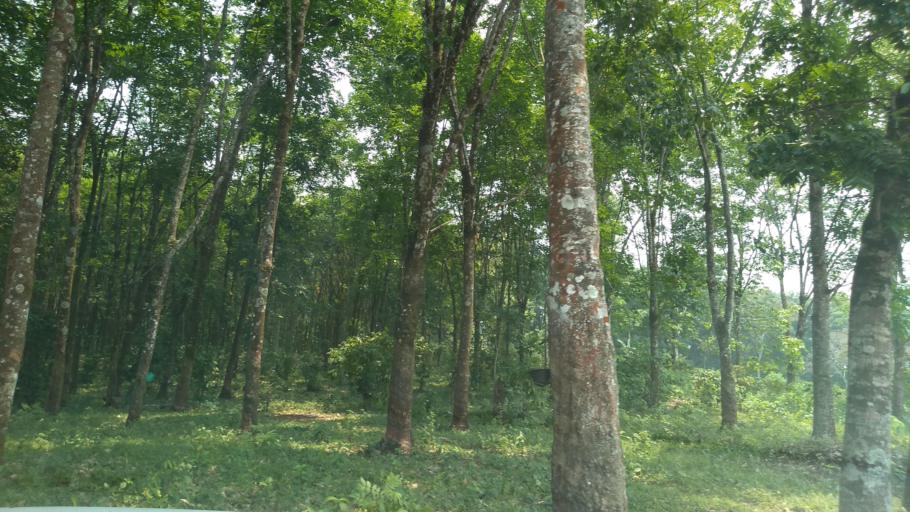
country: MX
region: Veracruz
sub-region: Tezonapa
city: Laguna Chica (Pueblo Nuevo)
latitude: 18.5124
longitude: -96.7400
